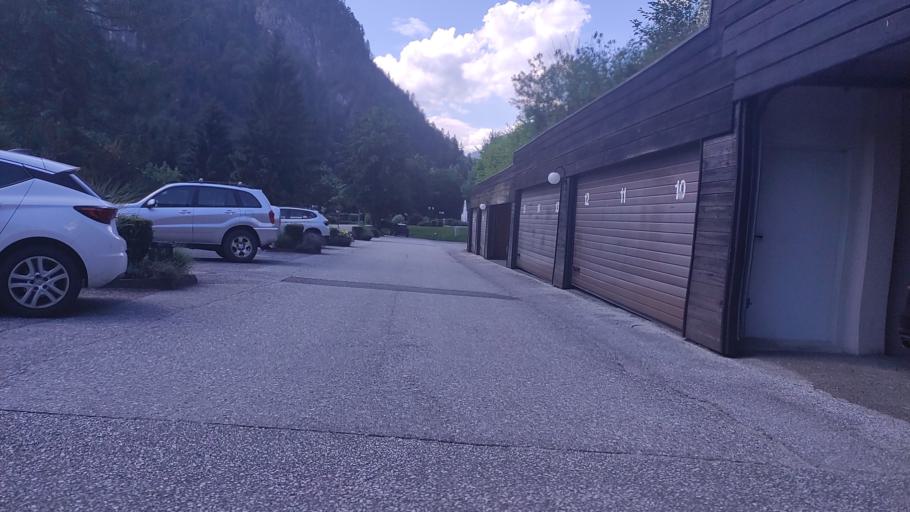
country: AT
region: Salzburg
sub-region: Politischer Bezirk Zell am See
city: Saalfelden am Steinernen Meer
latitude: 47.4814
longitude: 12.8314
